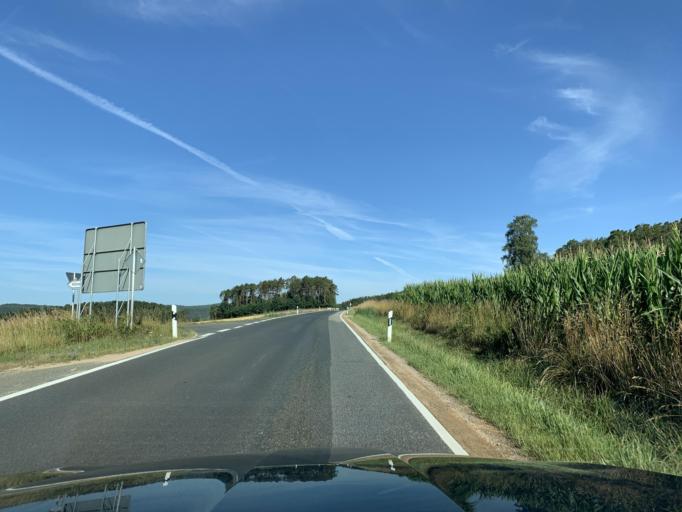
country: DE
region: Bavaria
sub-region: Upper Palatinate
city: Pettendorf
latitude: 49.3604
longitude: 12.3724
